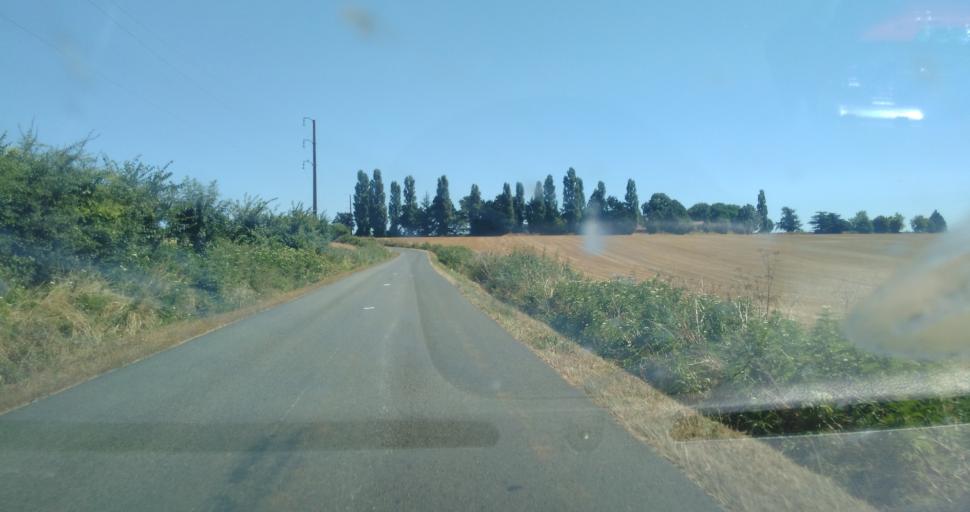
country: FR
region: Pays de la Loire
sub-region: Departement de la Vendee
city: Sainte-Hermine
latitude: 46.5774
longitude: -1.0459
